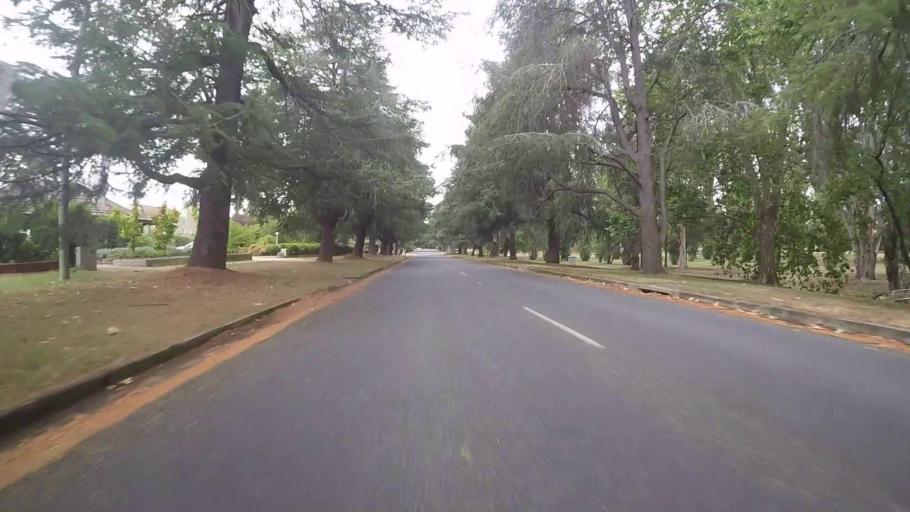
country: AU
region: Australian Capital Territory
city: Forrest
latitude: -35.3127
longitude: 149.1385
